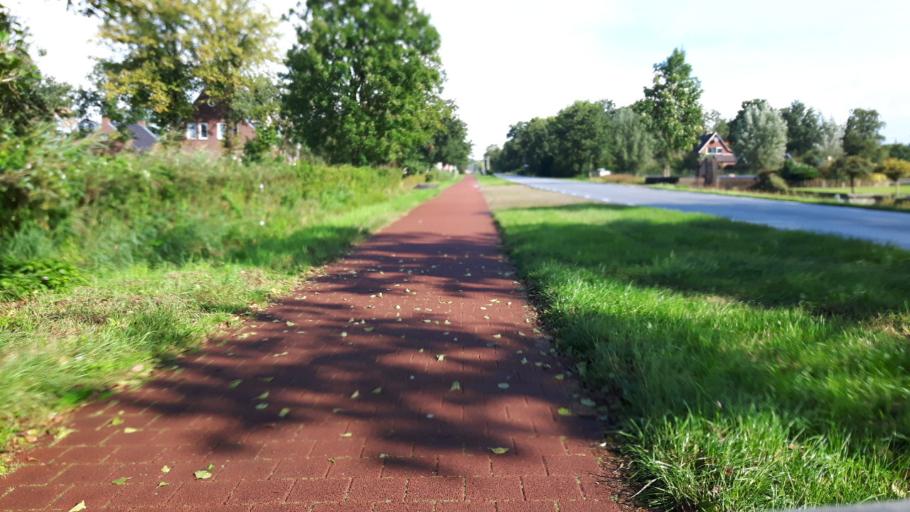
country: NL
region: Friesland
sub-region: Gemeente Smallingerland
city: Drachten
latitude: 53.0835
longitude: 6.0998
